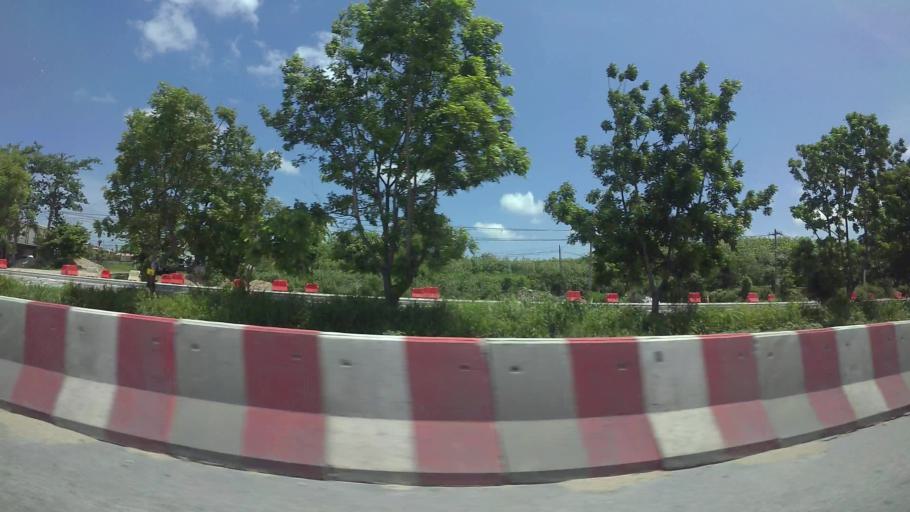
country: TH
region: Rayong
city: Rayong
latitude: 12.7245
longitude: 101.2180
